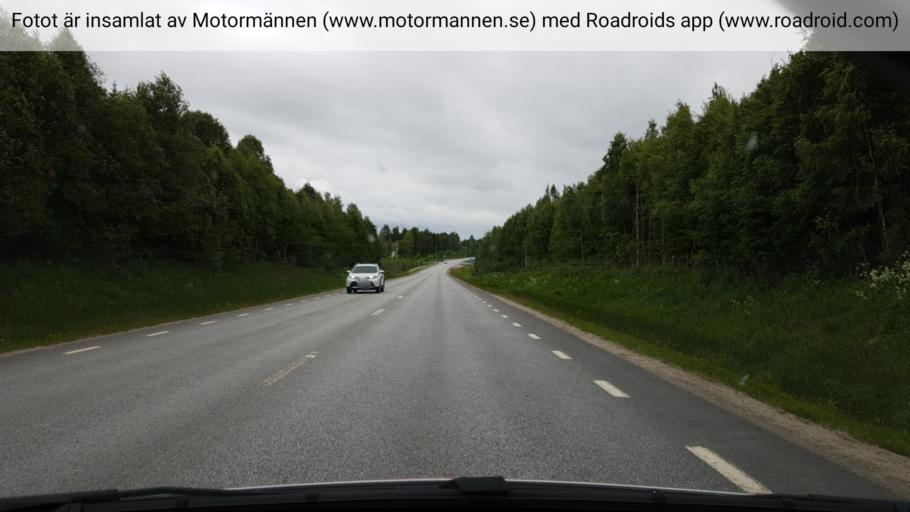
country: SE
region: Vaesterbotten
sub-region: Vannas Kommun
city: Vaennaes
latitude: 63.9952
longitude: 19.7275
